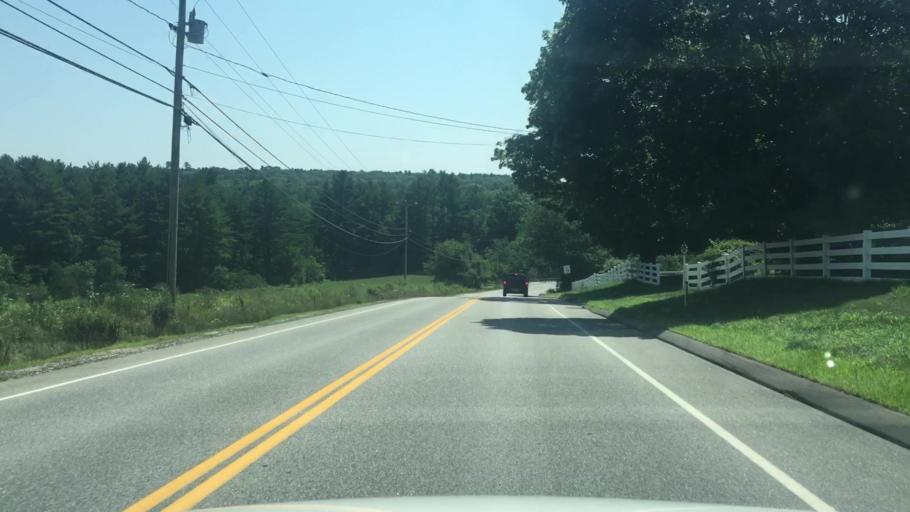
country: US
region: Maine
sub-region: Cumberland County
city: Cumberland Center
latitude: 43.8184
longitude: -70.2935
